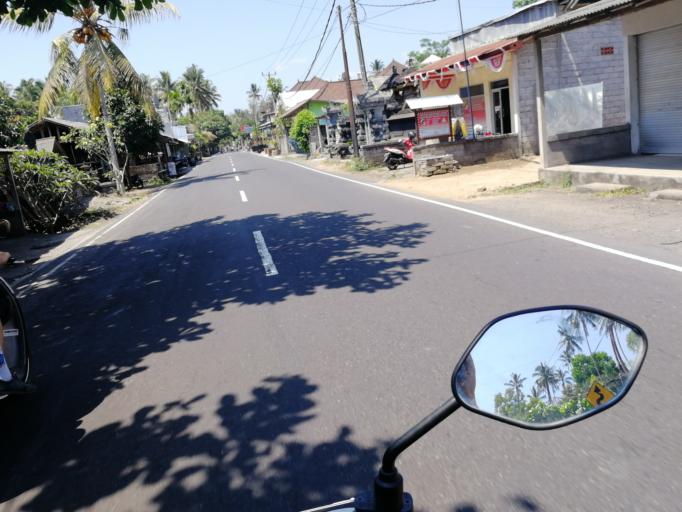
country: ID
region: Bali
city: Abang
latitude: -8.3936
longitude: 115.5978
